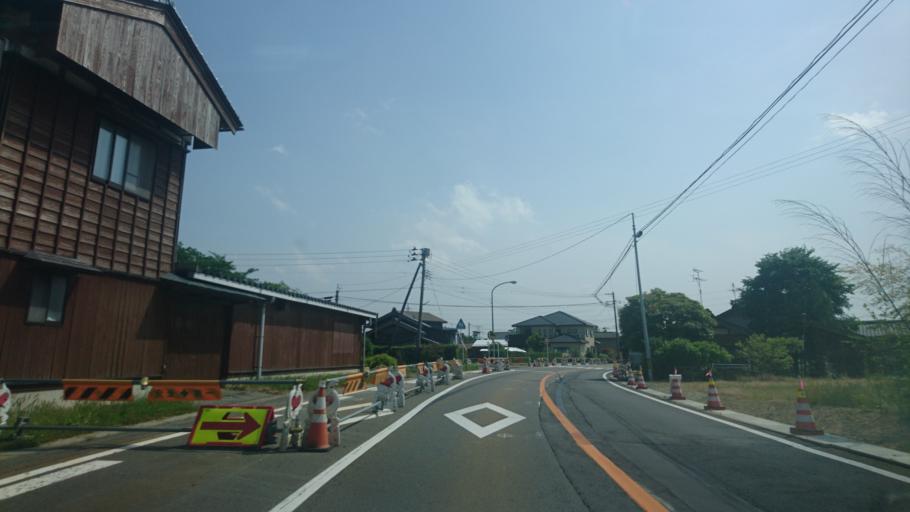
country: JP
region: Niigata
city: Shibata
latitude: 37.9836
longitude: 139.2923
